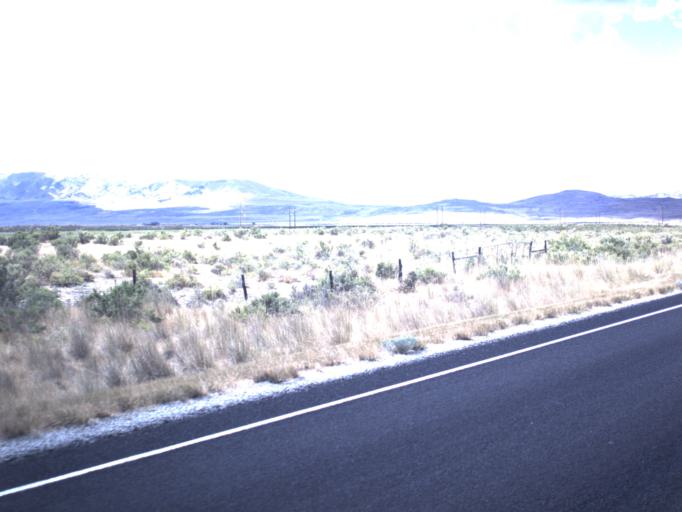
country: US
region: Utah
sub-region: Box Elder County
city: Tremonton
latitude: 41.6250
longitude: -112.3939
